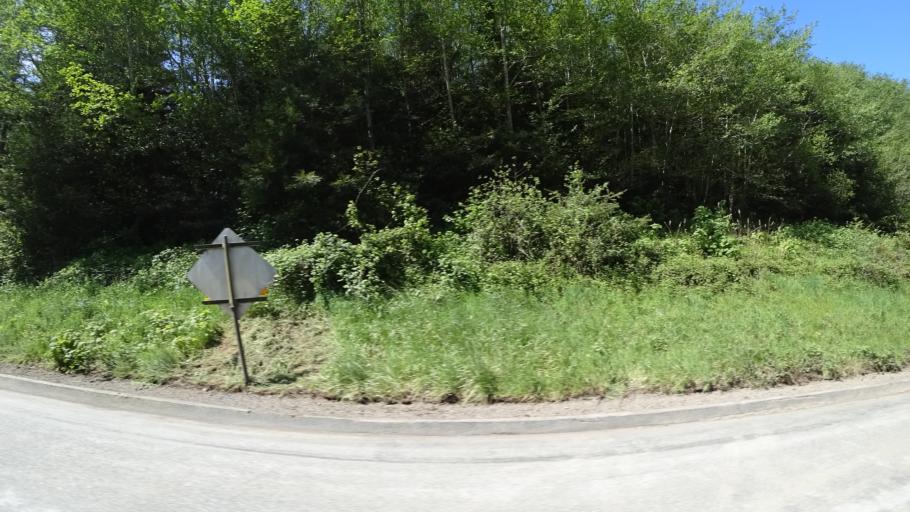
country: US
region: California
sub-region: Del Norte County
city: Bertsch-Oceanview
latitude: 41.4614
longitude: -124.0349
